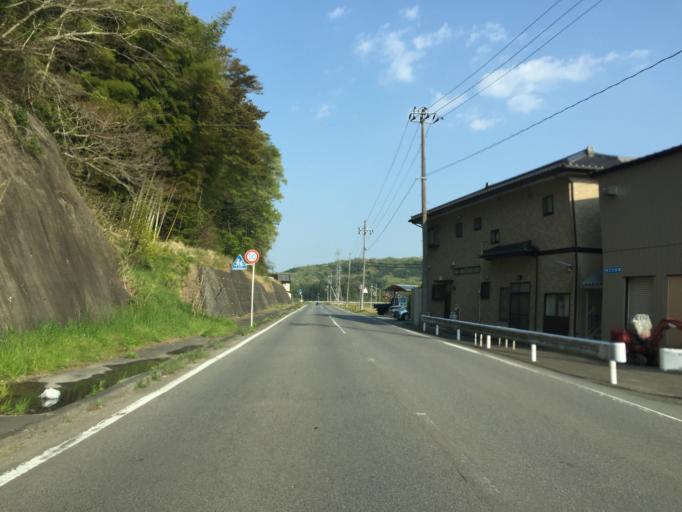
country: JP
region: Fukushima
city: Iwaki
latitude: 36.9576
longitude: 140.8208
